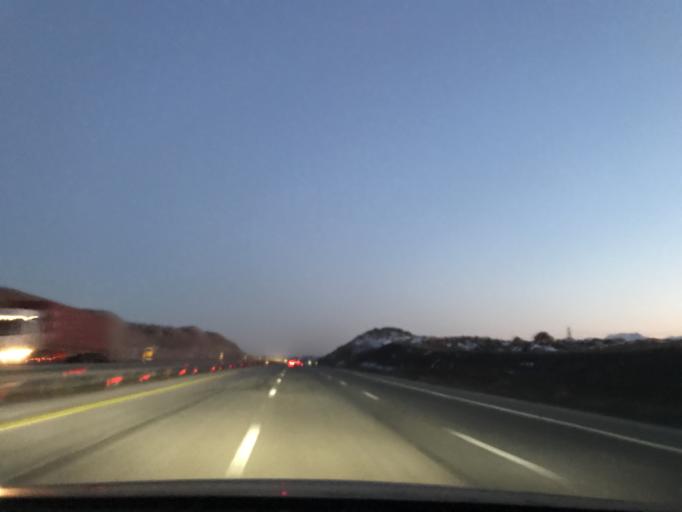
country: IR
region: Isfahan
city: Kashan
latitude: 33.8095
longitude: 51.6447
